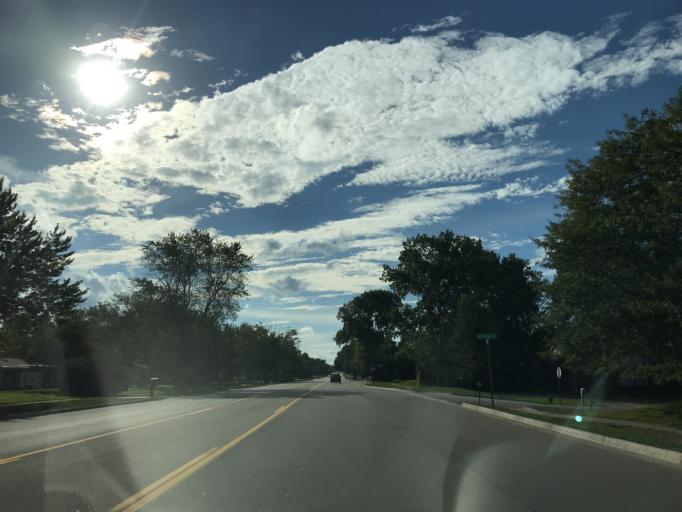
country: US
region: Michigan
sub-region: Oakland County
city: Farmington Hills
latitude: 42.5137
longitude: -83.3630
